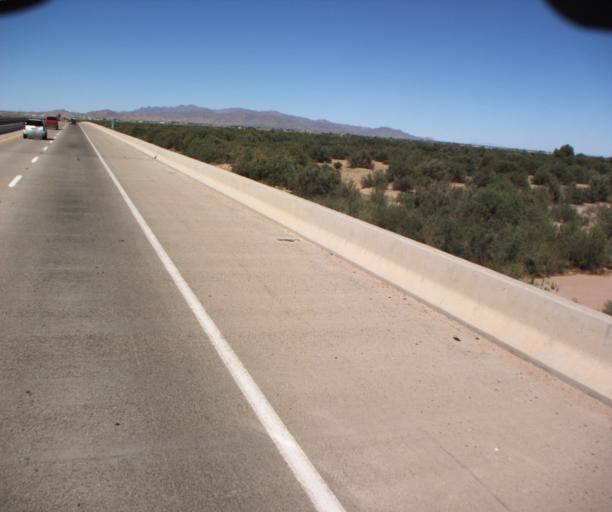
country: US
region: Arizona
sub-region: Maricopa County
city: Buckeye
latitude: 33.3333
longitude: -112.6233
